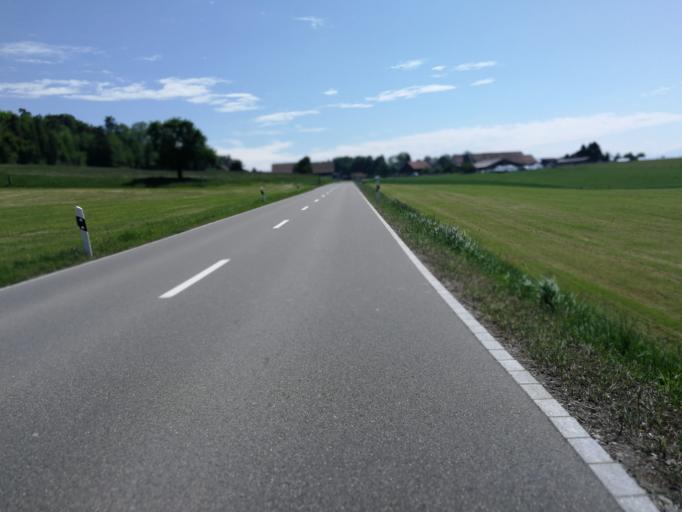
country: CH
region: Zurich
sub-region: Bezirk Uster
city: Aesch
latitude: 47.3088
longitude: 8.6383
